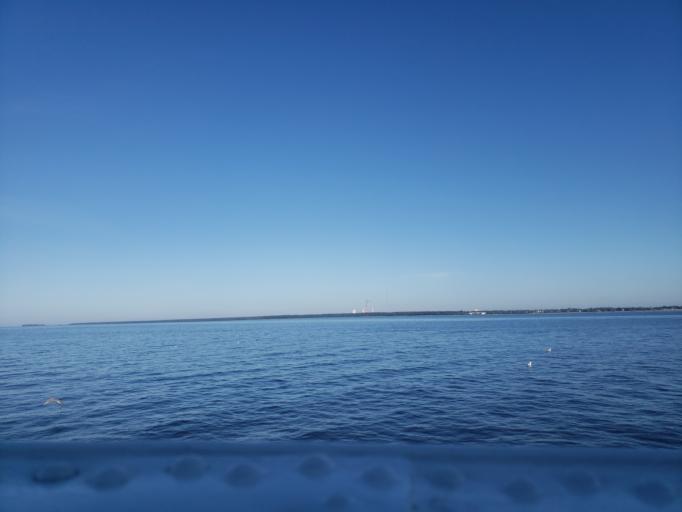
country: RU
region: St.-Petersburg
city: Lakhtinskiy
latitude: 59.9579
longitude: 30.1667
